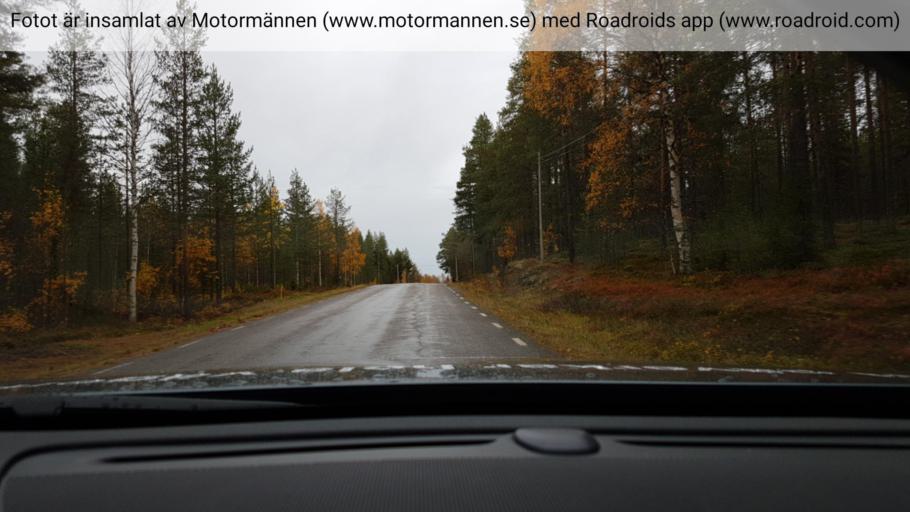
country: SE
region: Norrbotten
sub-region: Pajala Kommun
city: Pajala
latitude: 67.1502
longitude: 22.6551
